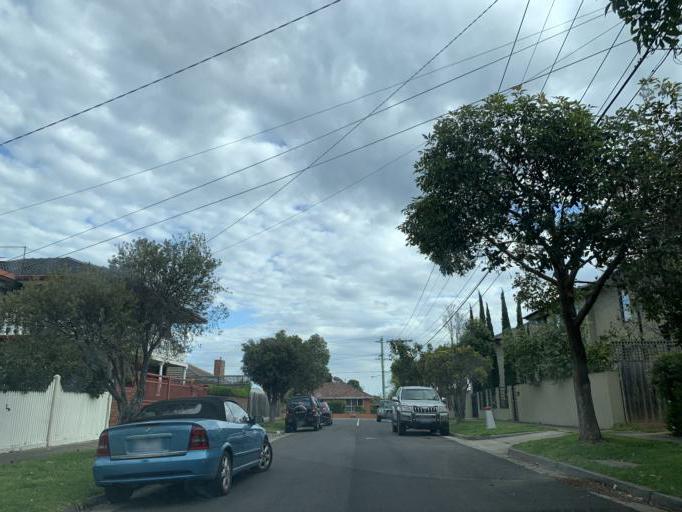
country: AU
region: Victoria
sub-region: Bayside
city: Hampton
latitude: -37.9444
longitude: 145.0120
